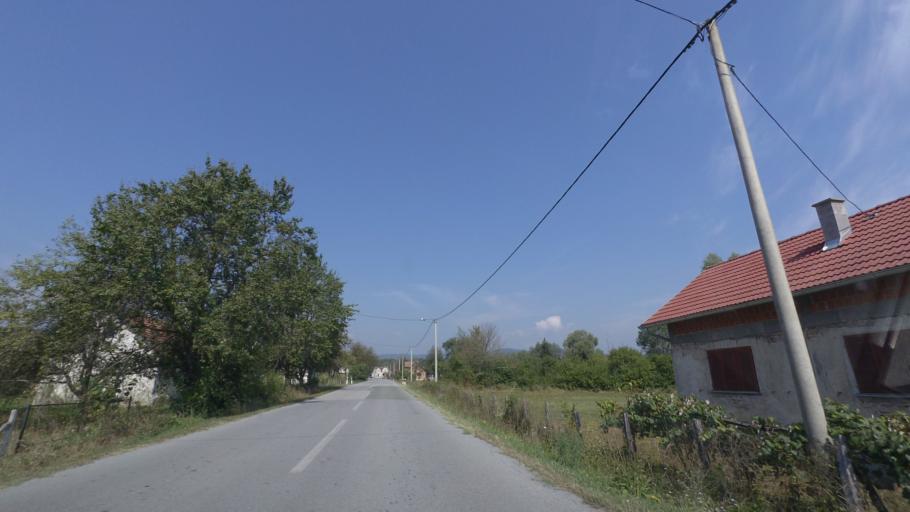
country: HR
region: Sisacko-Moslavacka
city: Dvor
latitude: 45.1127
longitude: 16.2772
